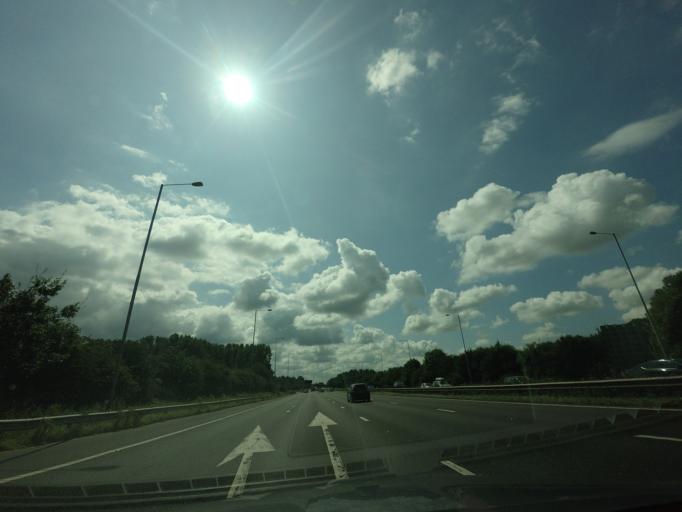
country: GB
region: England
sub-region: Lancashire
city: Clayton-le-Woods
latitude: 53.6972
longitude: -2.6774
